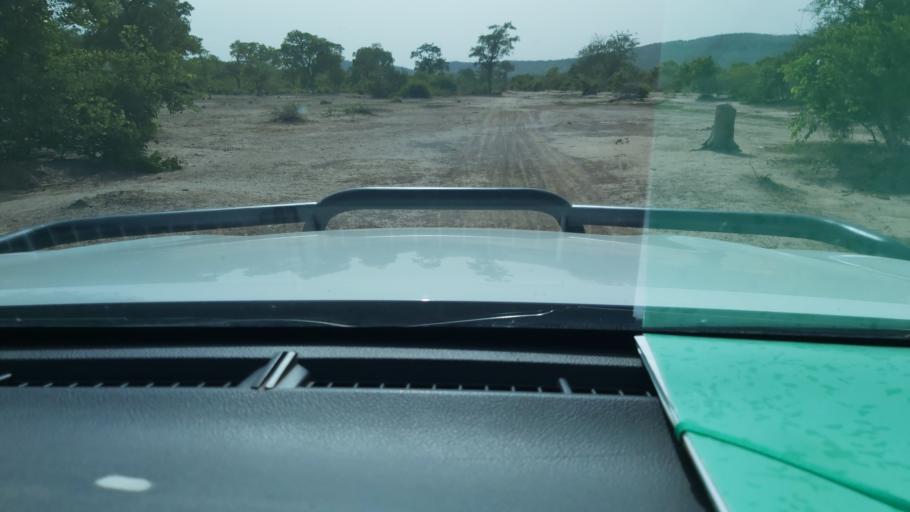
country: ML
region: Koulikoro
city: Koulikoro
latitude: 13.1748
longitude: -7.7402
